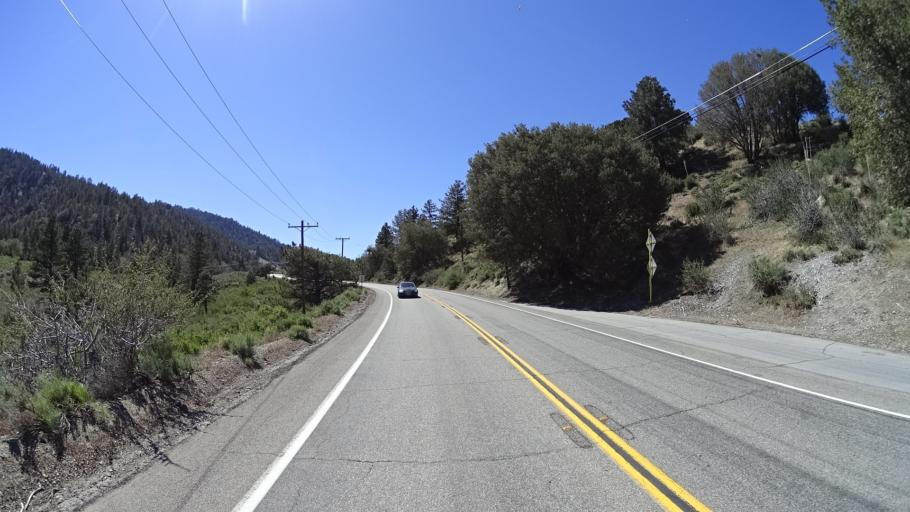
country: US
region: California
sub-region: San Bernardino County
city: Wrightwood
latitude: 34.3709
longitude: -117.6665
